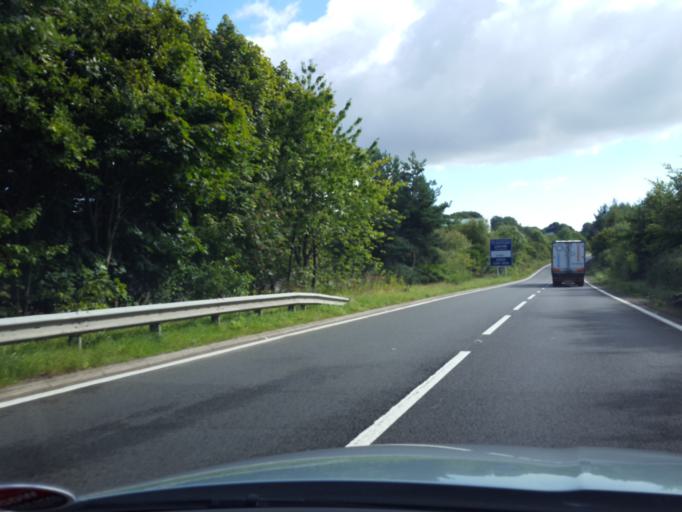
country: GB
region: Scotland
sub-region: Fife
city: Rosyth
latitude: 56.0474
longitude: -3.4277
